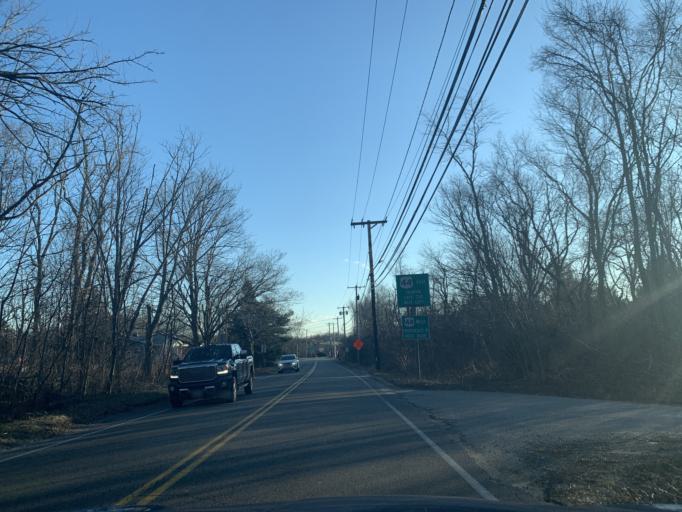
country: US
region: Massachusetts
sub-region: Bristol County
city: Rehoboth
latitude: 41.8567
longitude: -71.2387
